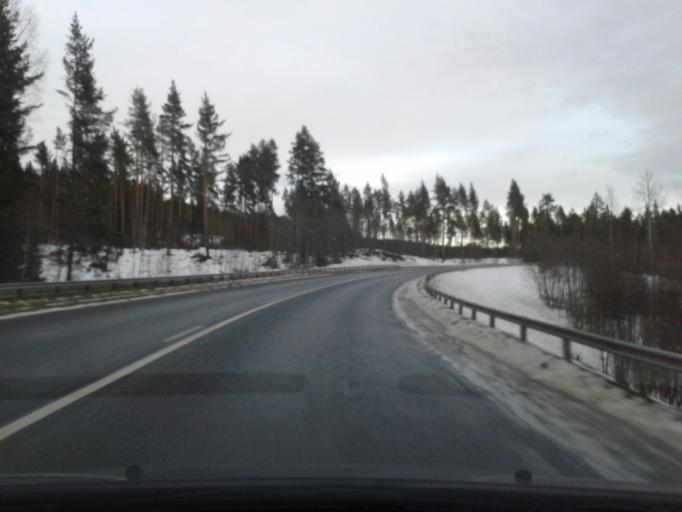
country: SE
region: Vaesternorrland
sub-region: Solleftea Kommun
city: Solleftea
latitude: 63.3345
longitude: 17.1318
